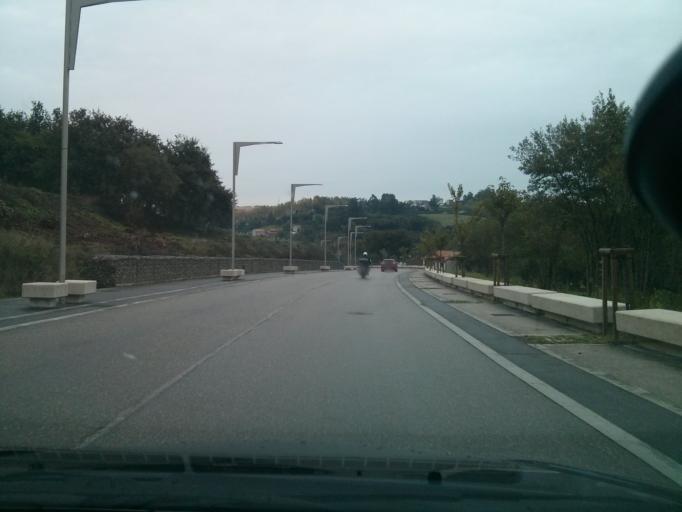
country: ES
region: Galicia
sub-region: Provincia da Coruna
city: Santiago de Compostela
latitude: 42.8736
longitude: -8.5249
